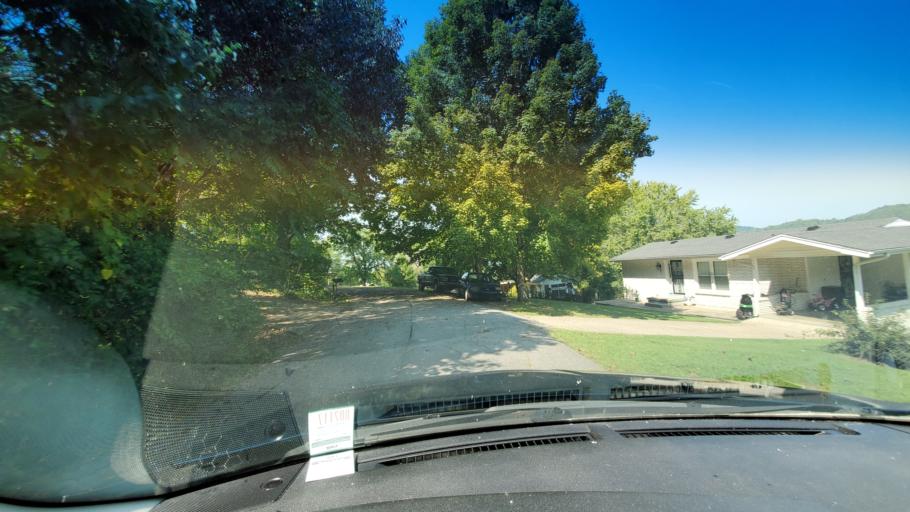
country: US
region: Tennessee
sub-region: Smith County
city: Carthage
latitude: 36.2512
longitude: -85.9619
